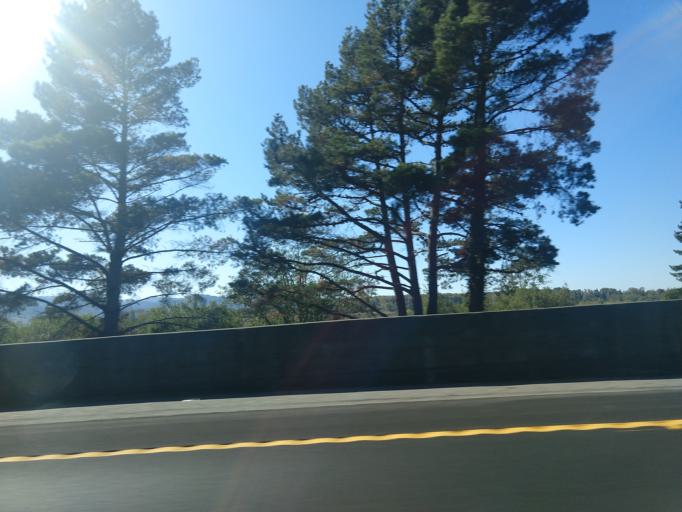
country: US
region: California
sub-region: Humboldt County
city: Fortuna
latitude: 40.5740
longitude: -124.1489
